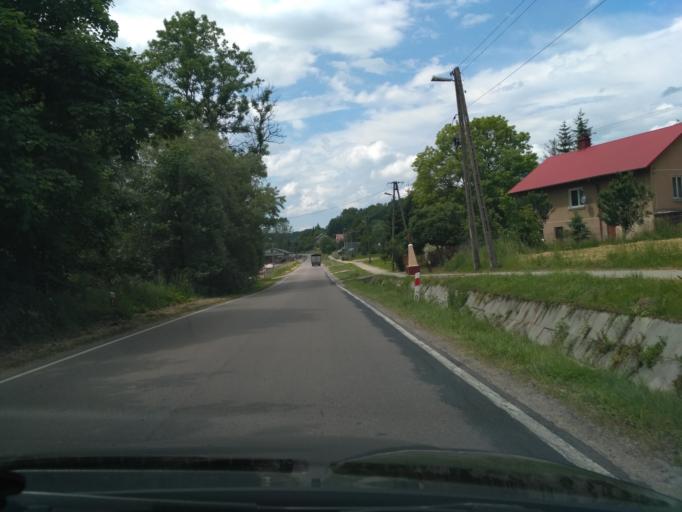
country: PL
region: Subcarpathian Voivodeship
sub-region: Powiat przeworski
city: Jawornik Polski
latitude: 49.8886
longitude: 22.2763
